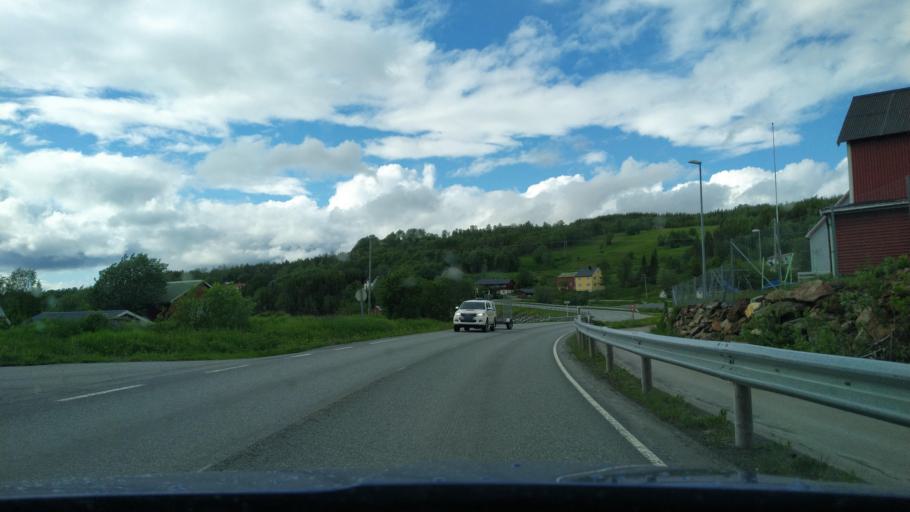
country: NO
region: Troms
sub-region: Sorreisa
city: Sorreisa
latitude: 69.1749
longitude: 18.0832
